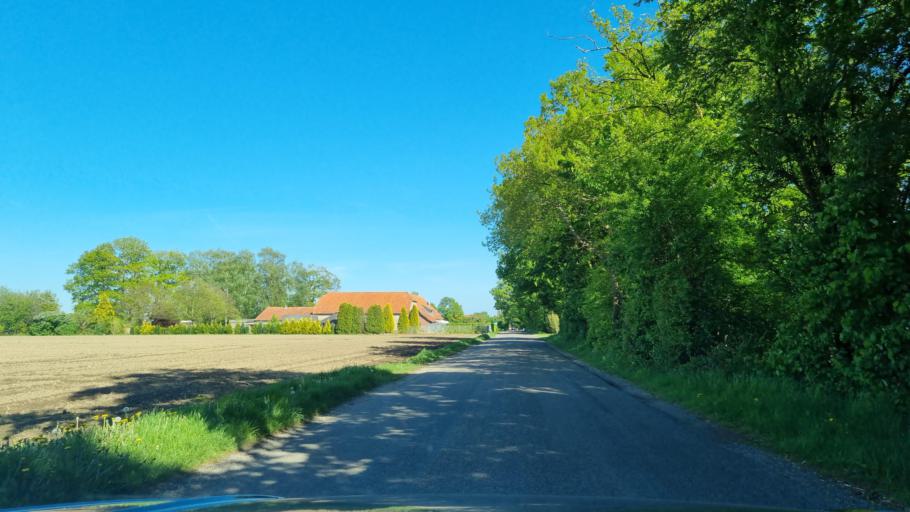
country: DE
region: North Rhine-Westphalia
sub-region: Regierungsbezirk Dusseldorf
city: Kleve
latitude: 51.7518
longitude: 6.1061
